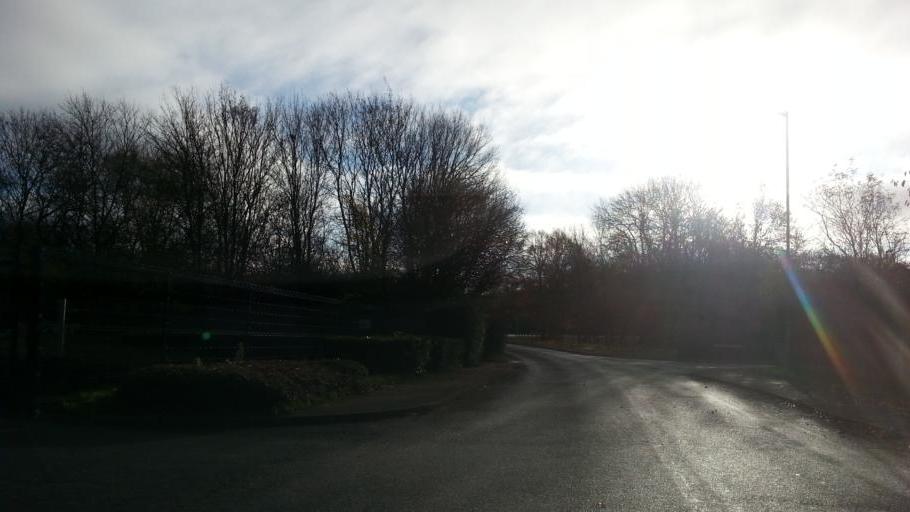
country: GB
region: England
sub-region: Suffolk
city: Wickham Market
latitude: 52.1311
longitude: 1.4229
